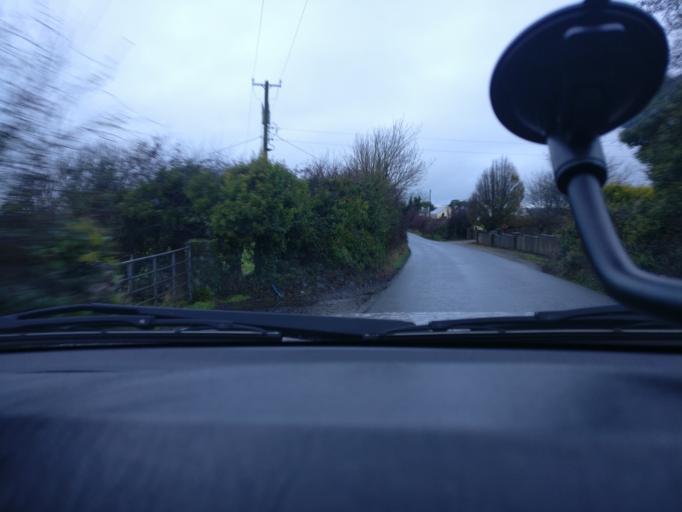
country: IE
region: Connaught
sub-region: County Galway
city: Loughrea
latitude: 53.2511
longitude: -8.5802
